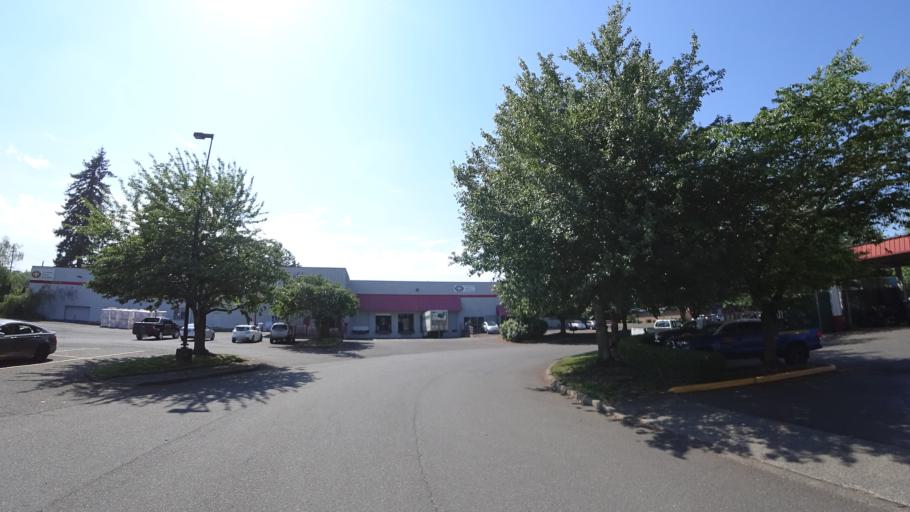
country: US
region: Oregon
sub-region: Multnomah County
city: Lents
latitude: 45.5586
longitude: -122.5390
